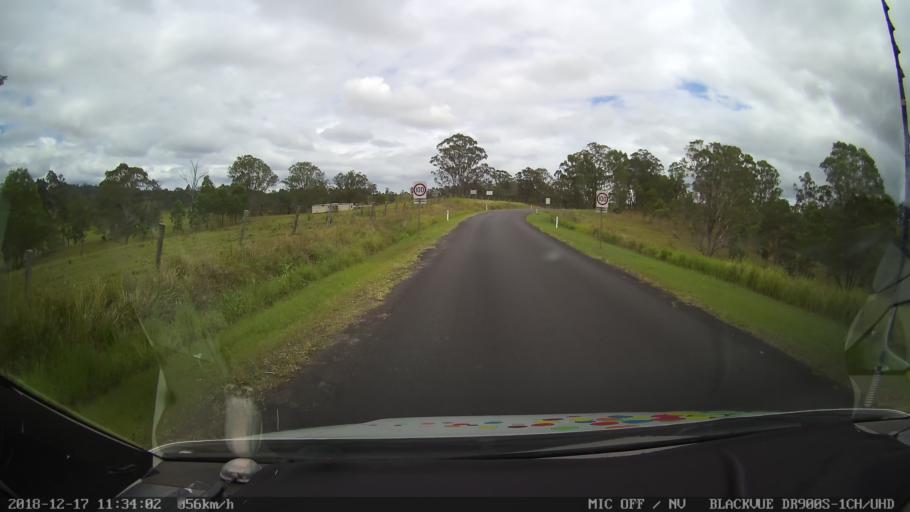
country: AU
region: New South Wales
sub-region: Kyogle
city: Kyogle
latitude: -28.7292
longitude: 152.6166
